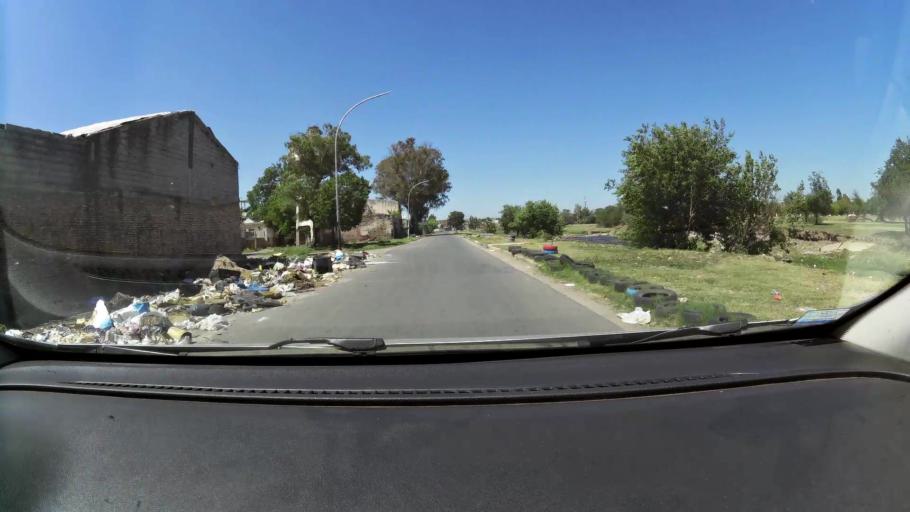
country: AR
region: Cordoba
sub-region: Departamento de Capital
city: Cordoba
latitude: -31.4140
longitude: -64.1416
